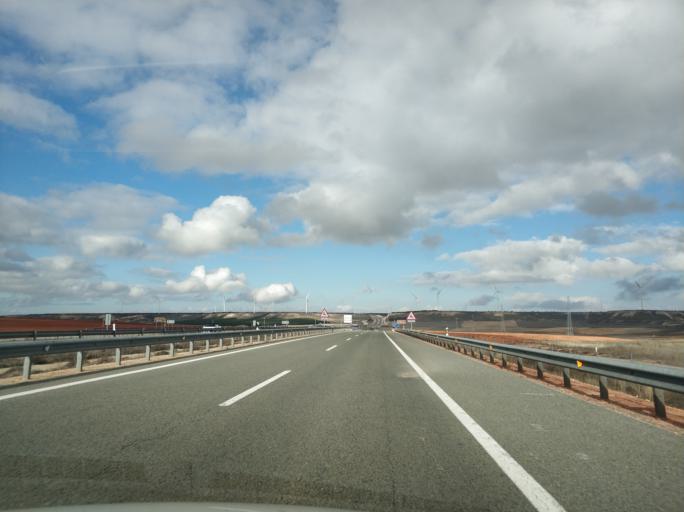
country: ES
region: Castille and Leon
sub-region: Provincia de Soria
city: Alcubilla de las Penas
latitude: 41.2683
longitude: -2.4742
